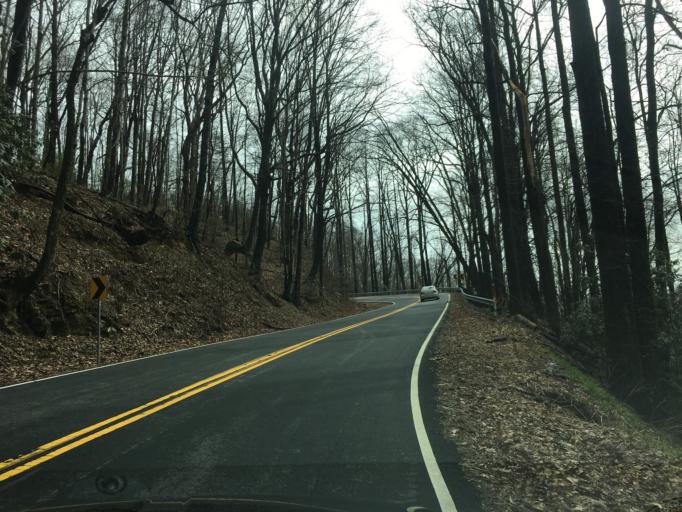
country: US
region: South Carolina
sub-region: Greenville County
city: Slater-Marietta
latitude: 35.1051
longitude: -82.6127
